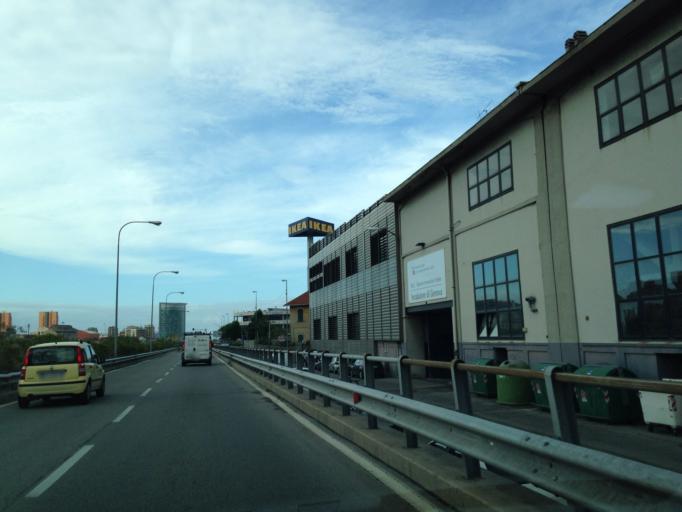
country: IT
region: Liguria
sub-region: Provincia di Genova
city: San Teodoro
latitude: 44.4246
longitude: 8.8864
